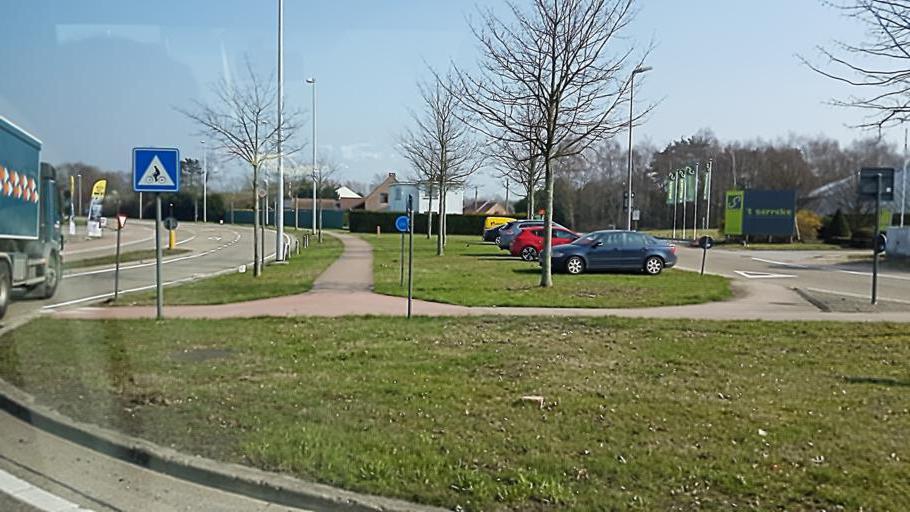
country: BE
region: Flanders
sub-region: Provincie Limburg
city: Tessenderlo
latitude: 51.0887
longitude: 5.1242
